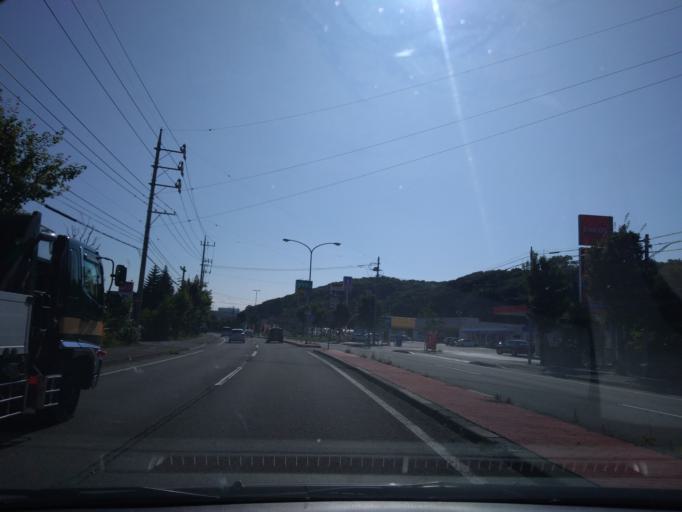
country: JP
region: Hokkaido
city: Kitahiroshima
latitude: 42.9821
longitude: 141.5539
